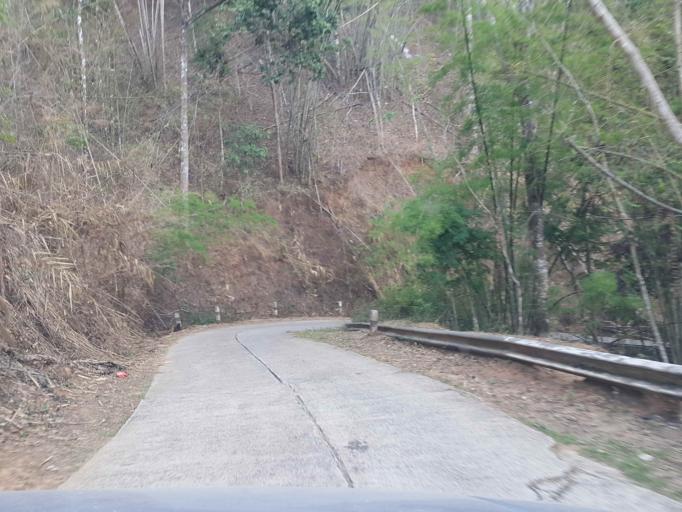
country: TH
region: Chiang Mai
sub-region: Amphoe Chiang Dao
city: Chiang Dao
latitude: 19.3860
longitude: 98.7711
